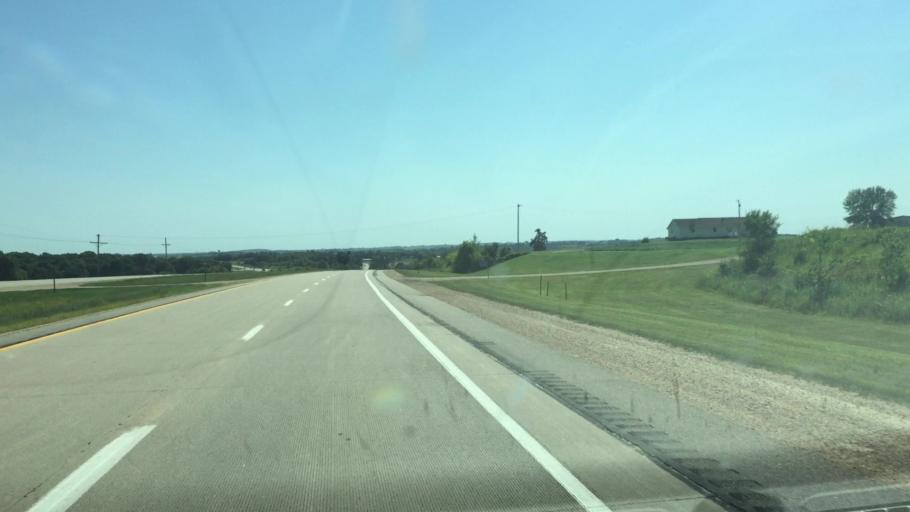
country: US
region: Iowa
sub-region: Jones County
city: Monticello
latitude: 42.2639
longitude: -91.1481
